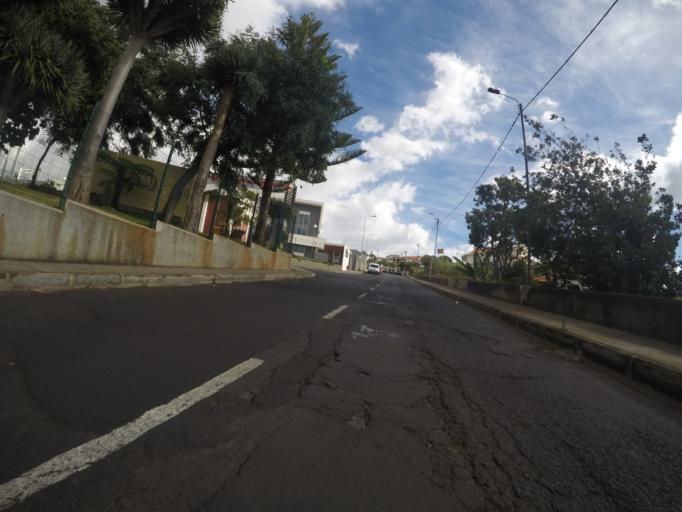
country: PT
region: Madeira
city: Camara de Lobos
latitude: 32.6508
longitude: -16.9458
